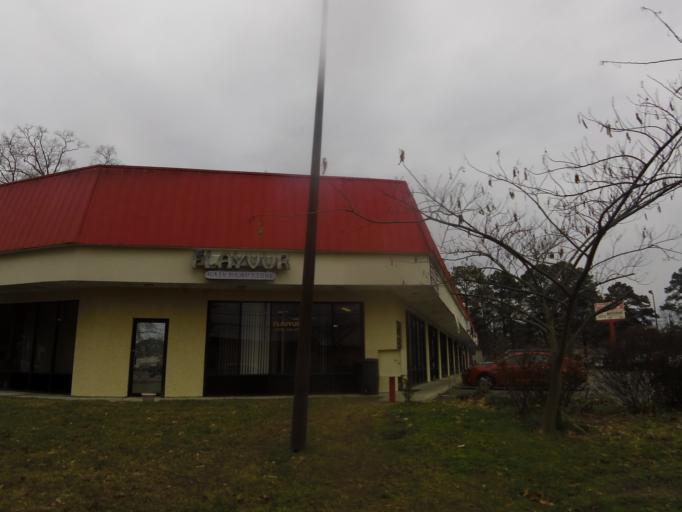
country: US
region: Virginia
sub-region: City of Portsmouth
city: Portsmouth Heights
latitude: 36.8650
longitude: -76.4034
